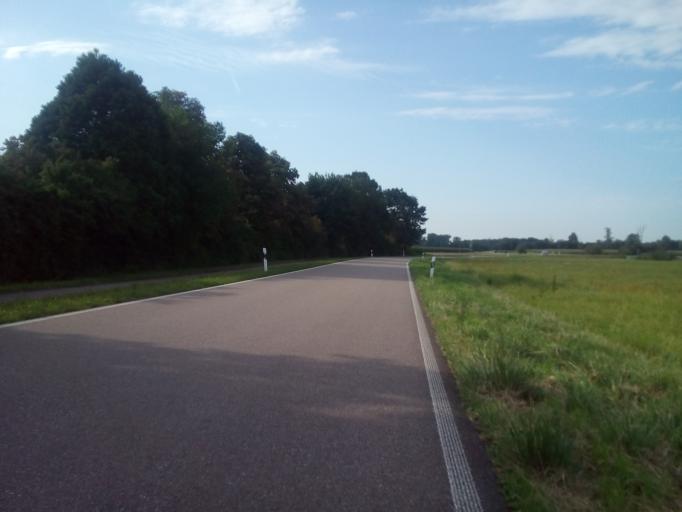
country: DE
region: Baden-Wuerttemberg
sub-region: Karlsruhe Region
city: Zell
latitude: 48.7255
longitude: 8.0652
